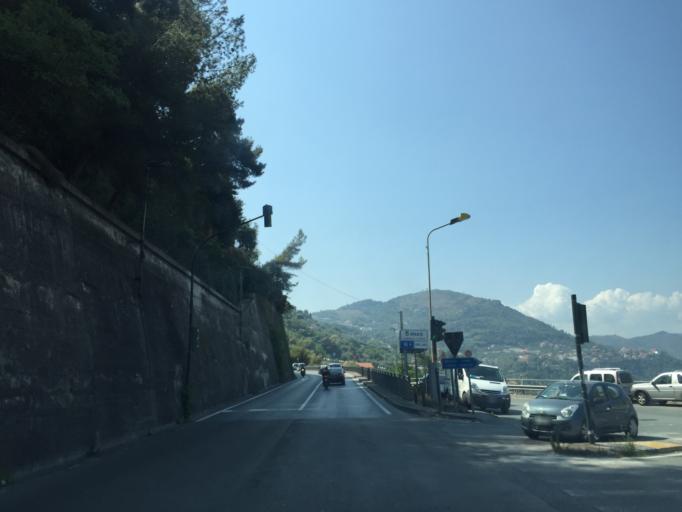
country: IT
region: Liguria
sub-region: Provincia di Imperia
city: Ventimiglia
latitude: 43.7941
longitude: 7.5975
